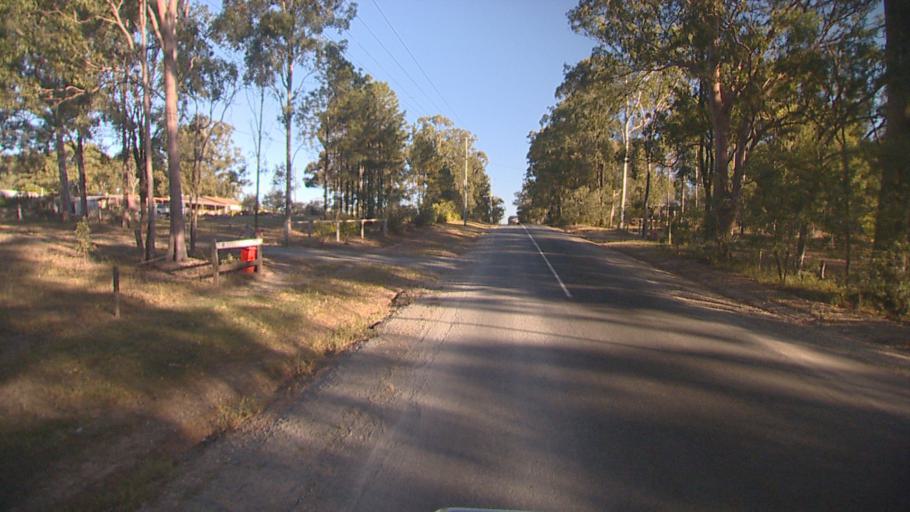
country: AU
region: Queensland
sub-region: Logan
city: Chambers Flat
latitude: -27.7766
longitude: 153.1363
